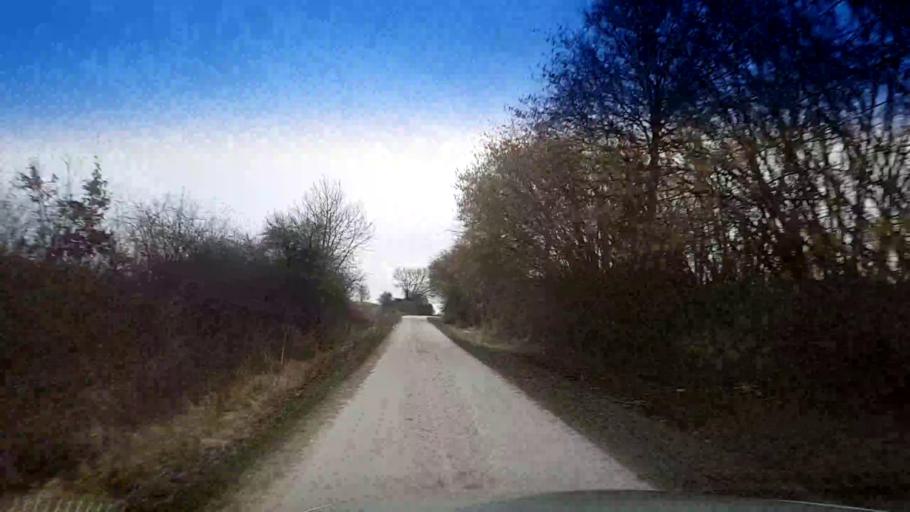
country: DE
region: Bavaria
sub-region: Upper Franconia
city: Pommersfelden
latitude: 49.8125
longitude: 10.8198
